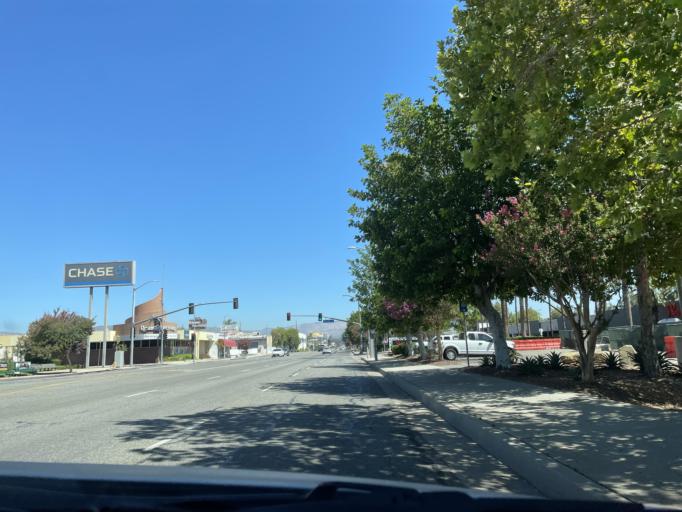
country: US
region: California
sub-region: Los Angeles County
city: Canoga Park
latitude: 34.1905
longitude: -118.6058
